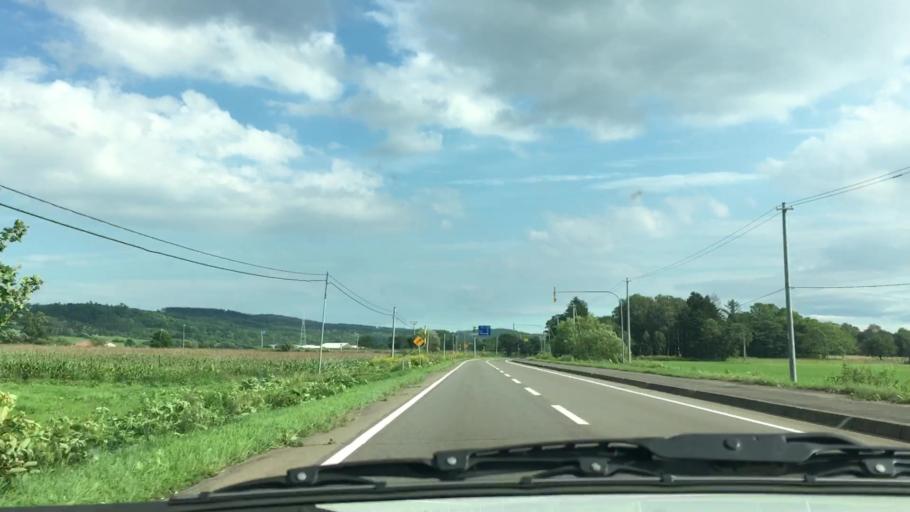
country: JP
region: Hokkaido
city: Otofuke
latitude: 43.3258
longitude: 143.2985
